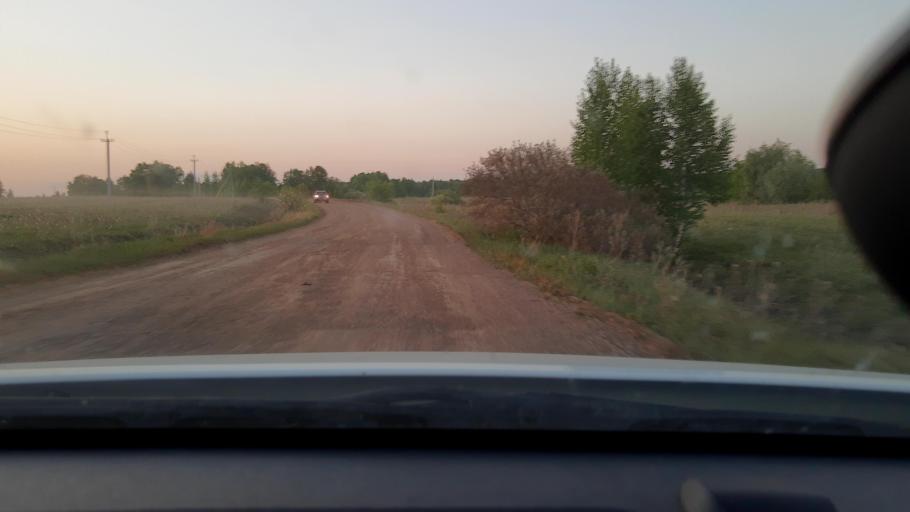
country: RU
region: Bashkortostan
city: Avdon
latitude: 54.5208
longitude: 55.8263
